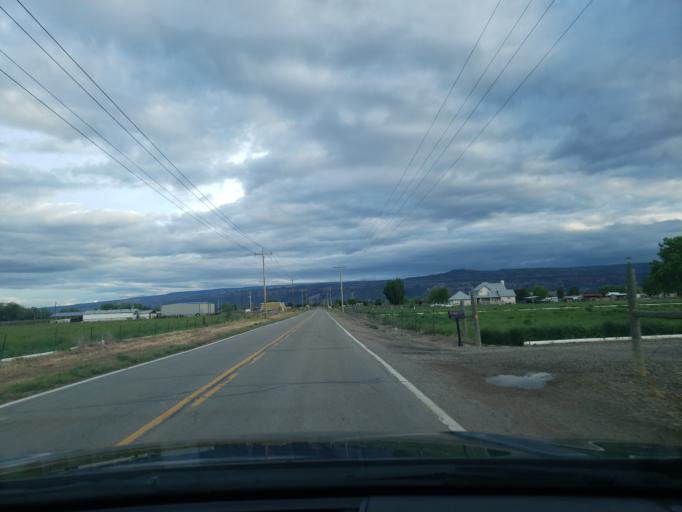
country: US
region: Colorado
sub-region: Mesa County
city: Fruita
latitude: 39.1922
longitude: -108.7013
